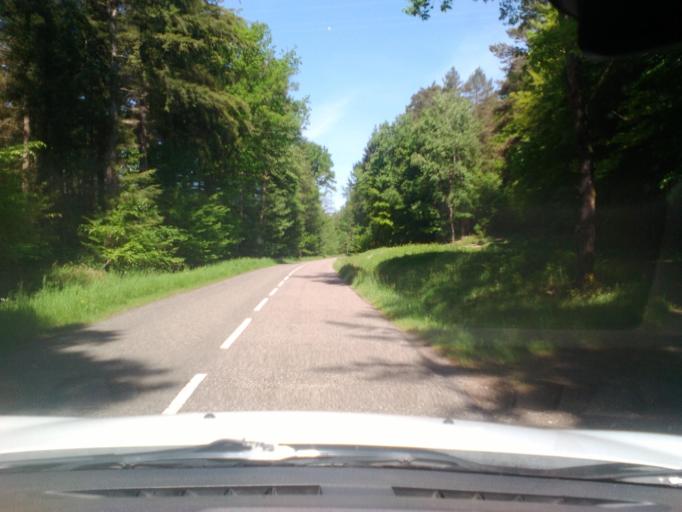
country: FR
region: Lorraine
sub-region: Departement des Vosges
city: Jeanmenil
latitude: 48.2758
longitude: 6.7124
